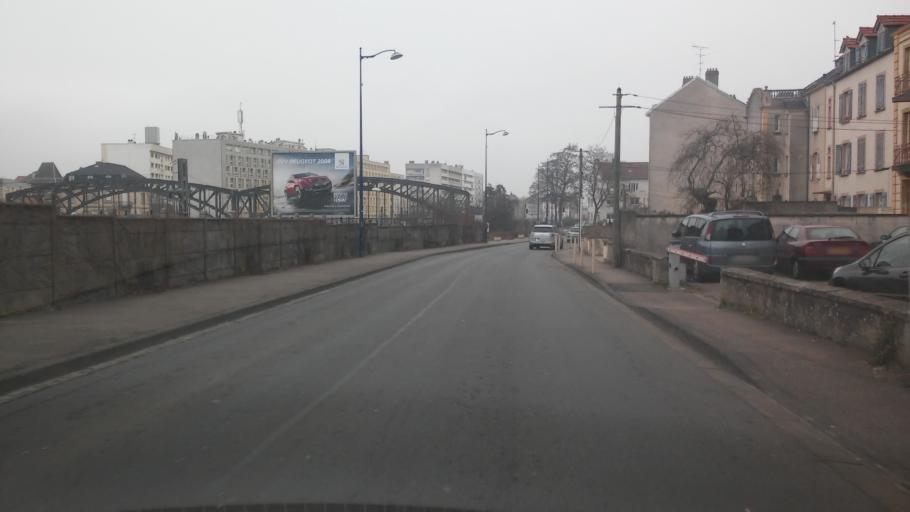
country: FR
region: Lorraine
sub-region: Departement de la Moselle
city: Montigny-les-Metz
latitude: 49.1005
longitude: 6.1689
